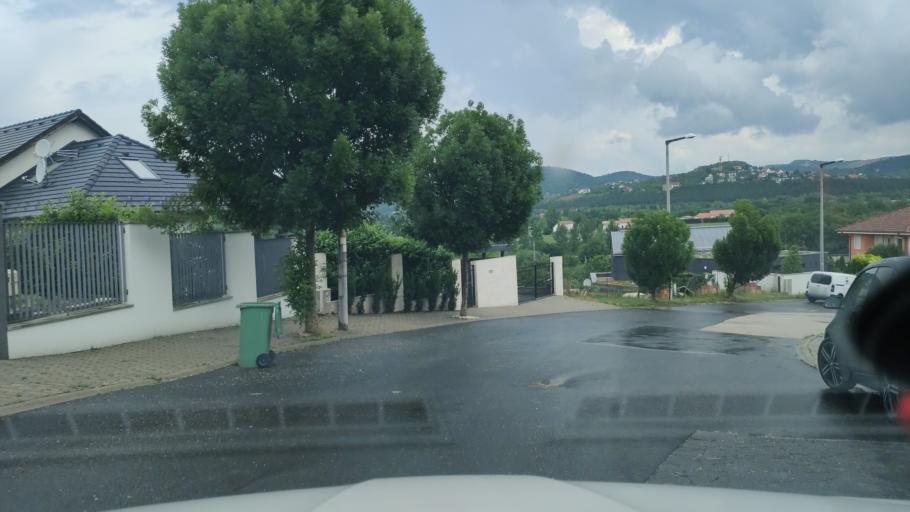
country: HU
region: Pest
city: Toeroekbalint
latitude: 47.4453
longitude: 18.9207
